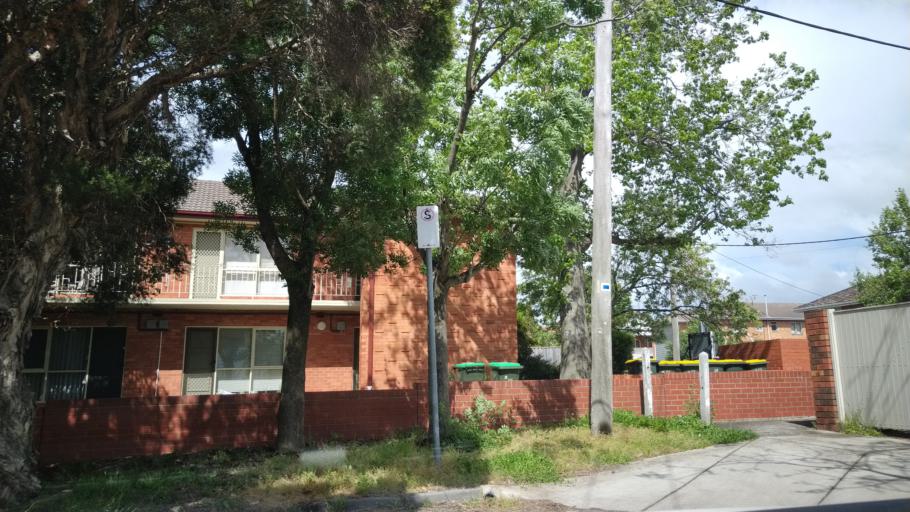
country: AU
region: Victoria
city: Caulfield North
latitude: -37.8778
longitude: 145.0327
